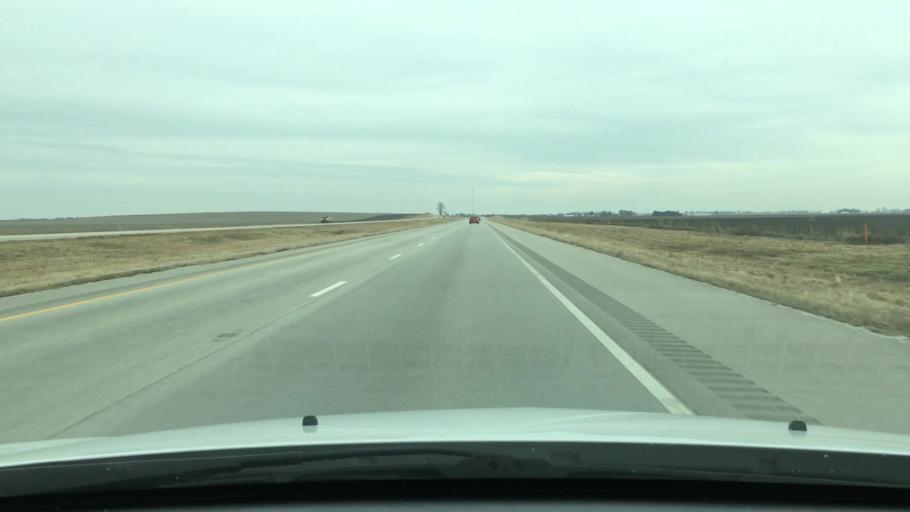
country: US
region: Illinois
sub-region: Morgan County
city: Jacksonville
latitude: 39.7381
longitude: -90.1078
